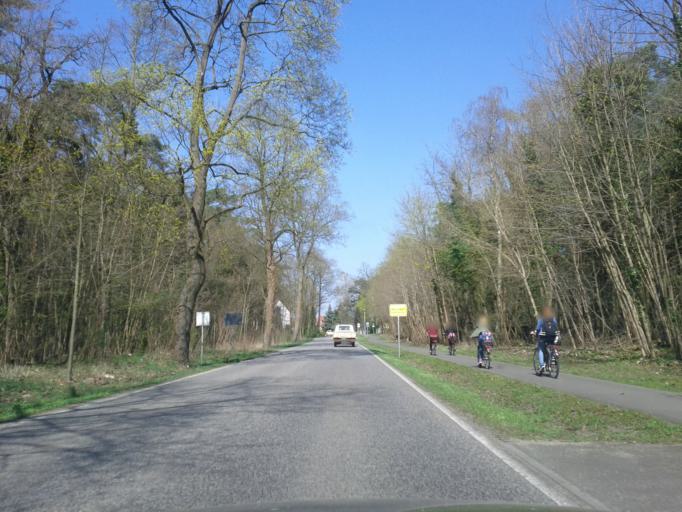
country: DE
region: Brandenburg
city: Woltersdorf
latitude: 52.4414
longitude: 13.7564
